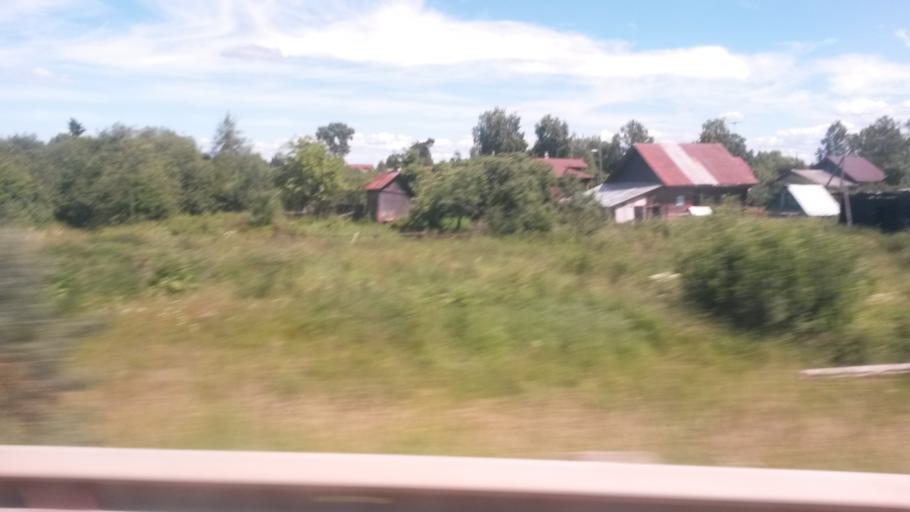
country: RU
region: Ivanovo
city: Staraya Vichuga
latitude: 57.2231
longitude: 41.8624
